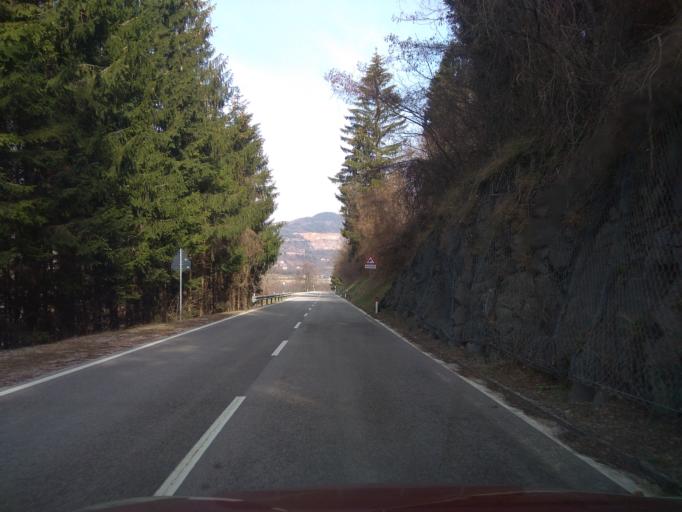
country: IT
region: Trentino-Alto Adige
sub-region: Provincia di Trento
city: Fornace
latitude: 46.1075
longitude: 11.2135
